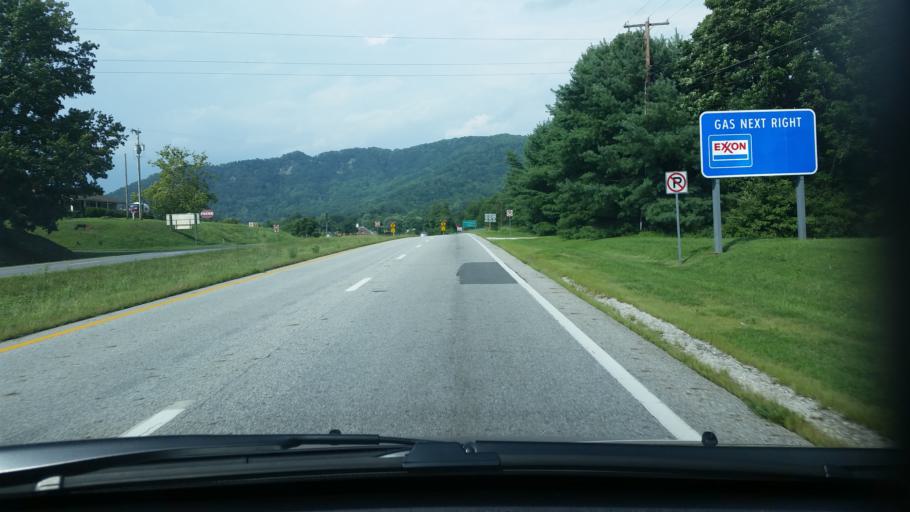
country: US
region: Virginia
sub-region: Nelson County
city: Lovingston
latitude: 37.7500
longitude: -78.8787
